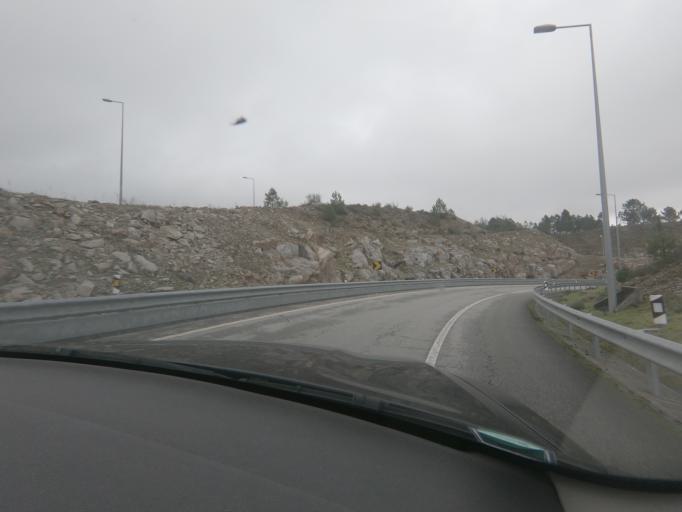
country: PT
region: Viseu
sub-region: Viseu
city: Abraveses
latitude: 40.6761
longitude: -7.9695
